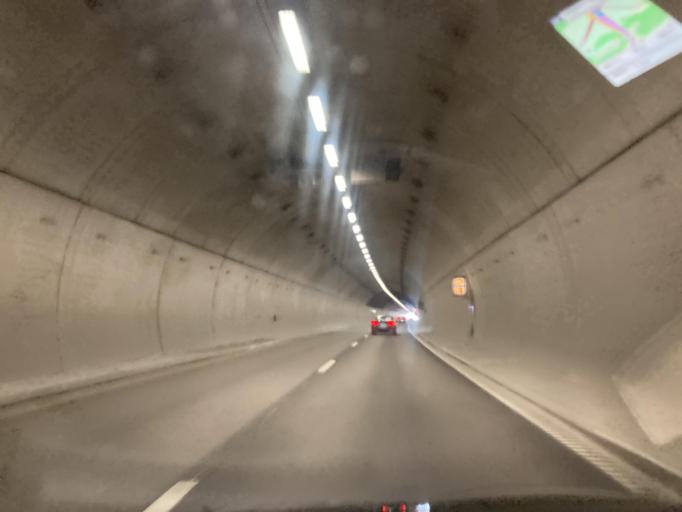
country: NO
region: Akershus
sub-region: Eidsvoll
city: Eidsvoll
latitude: 60.3415
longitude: 11.2036
